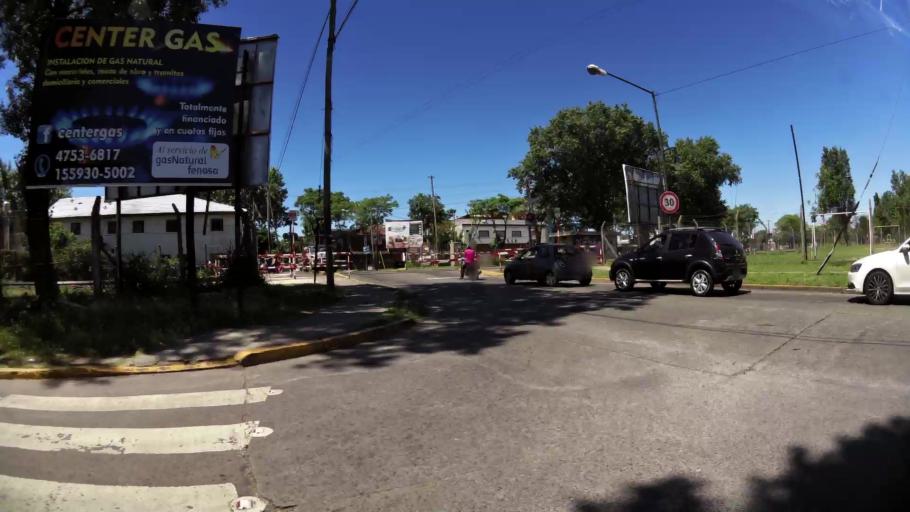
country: AR
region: Buenos Aires
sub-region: Partido de General San Martin
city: General San Martin
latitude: -34.5213
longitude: -58.5496
